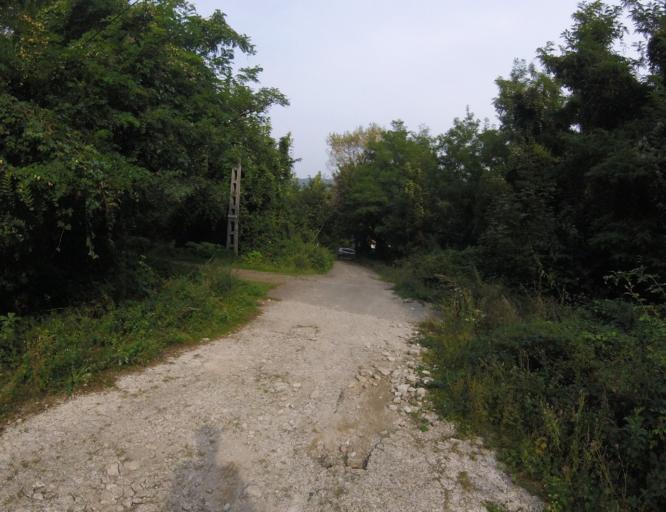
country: HU
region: Pest
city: Veroce
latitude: 47.8367
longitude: 19.0546
